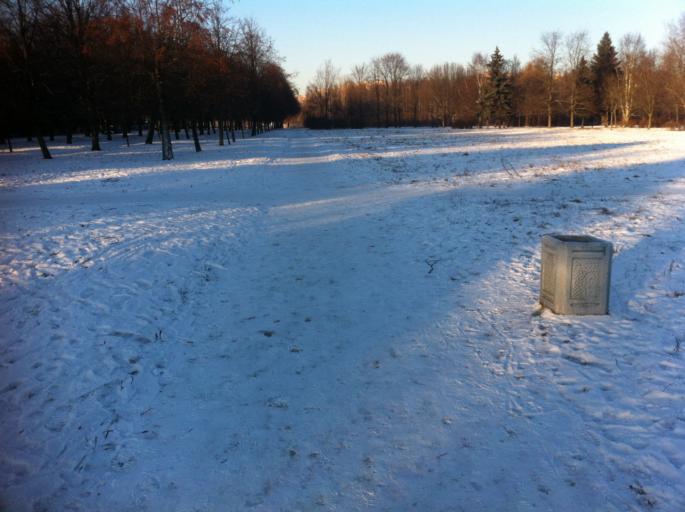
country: RU
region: St.-Petersburg
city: Uritsk
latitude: 59.8511
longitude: 30.1708
